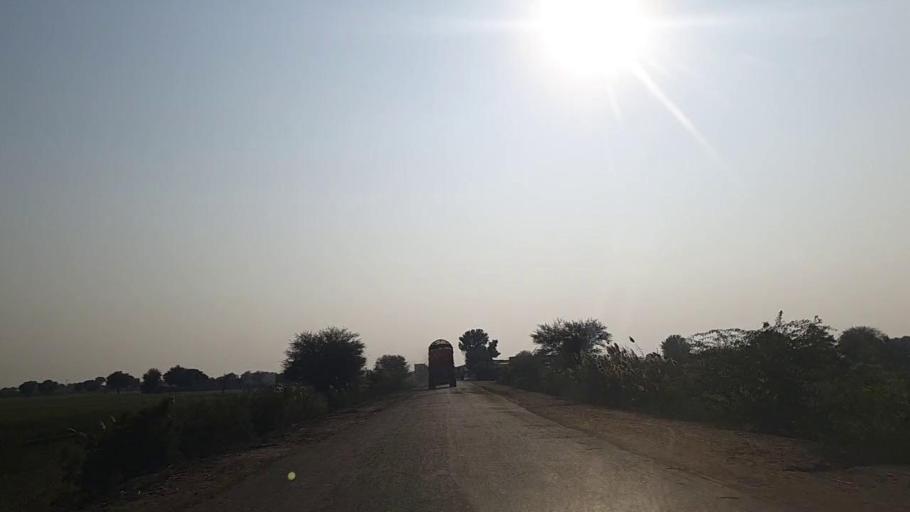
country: PK
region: Sindh
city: Jam Sahib
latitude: 26.2731
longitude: 68.6133
